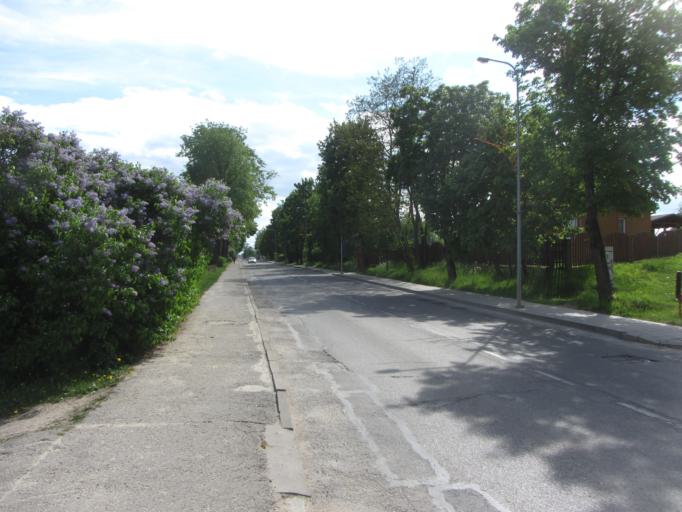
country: LT
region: Utenos apskritis
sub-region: Utena
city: Utena
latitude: 55.4931
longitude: 25.5887
